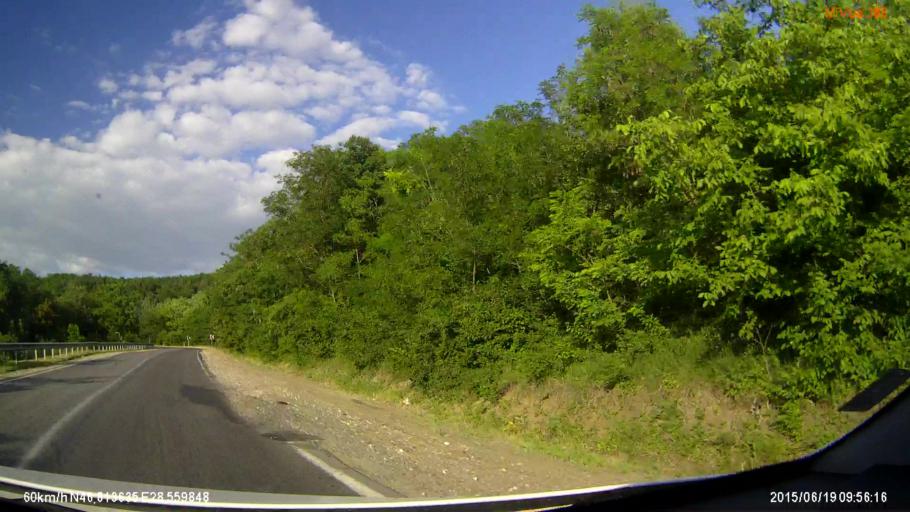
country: MD
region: Hincesti
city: Hincesti
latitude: 46.8134
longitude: 28.5595
